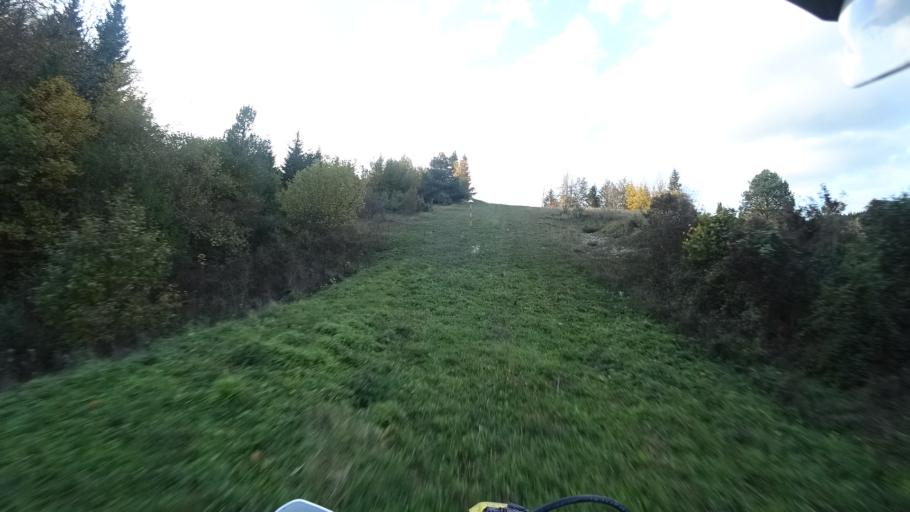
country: HR
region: Karlovacka
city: Plaski
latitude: 45.0070
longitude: 15.4242
